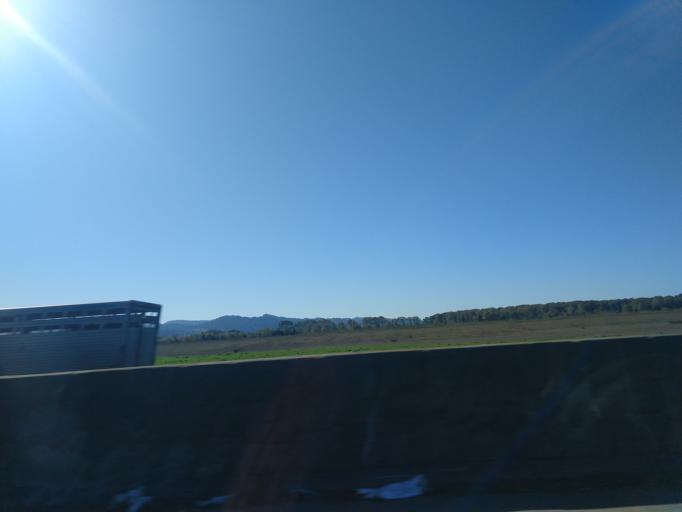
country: US
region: California
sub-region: Humboldt County
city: Fortuna
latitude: 40.5711
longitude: -124.1488
